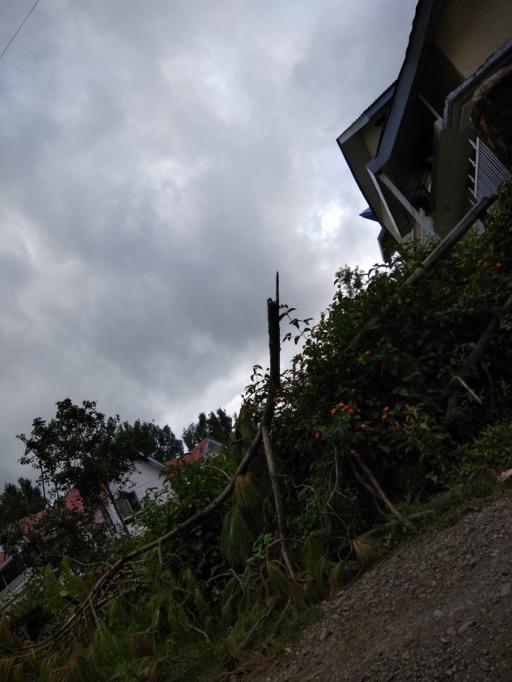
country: IN
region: Himachal Pradesh
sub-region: Kangra
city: Palampur
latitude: 32.1253
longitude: 76.5298
